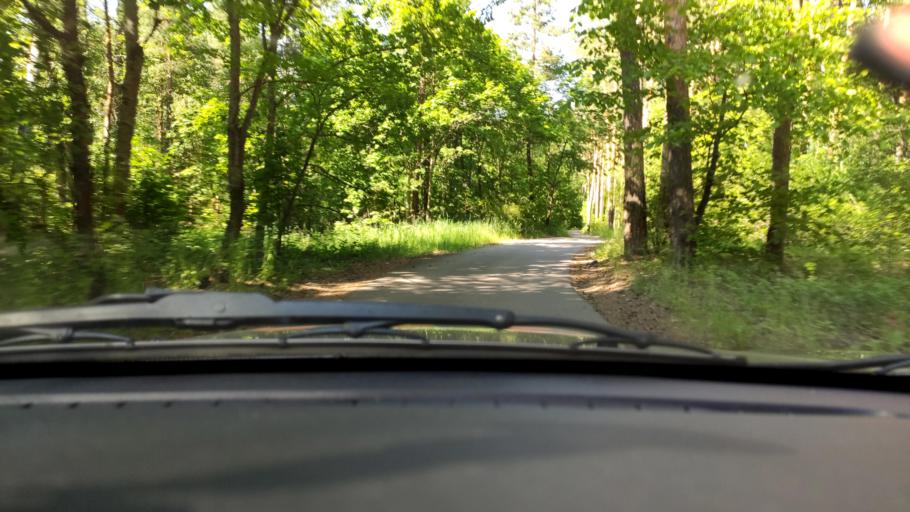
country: RU
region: Voronezj
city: Somovo
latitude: 51.8043
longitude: 39.3805
